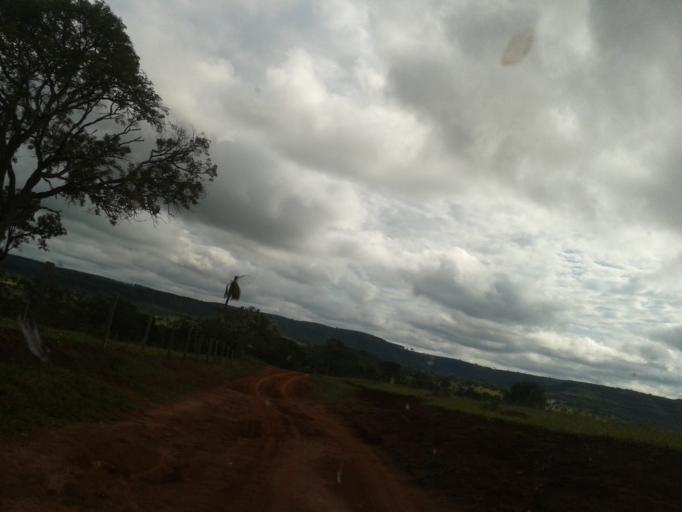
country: BR
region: Minas Gerais
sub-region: Campina Verde
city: Campina Verde
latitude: -19.4878
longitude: -49.6160
